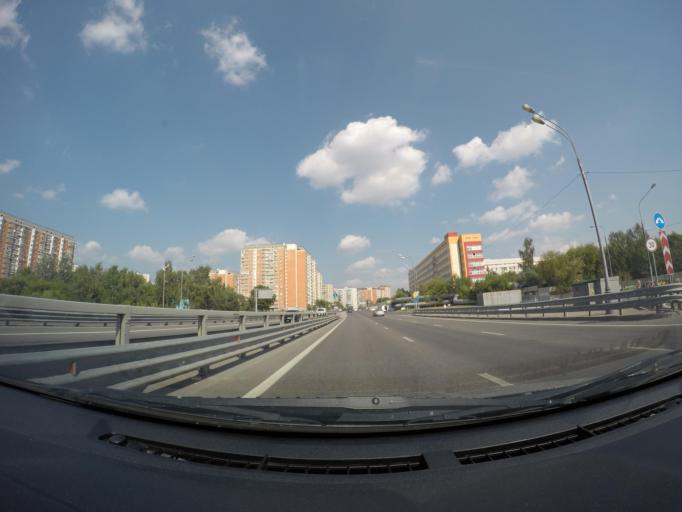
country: RU
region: Moscow
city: Zapadnoye Degunino
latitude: 55.8703
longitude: 37.5173
